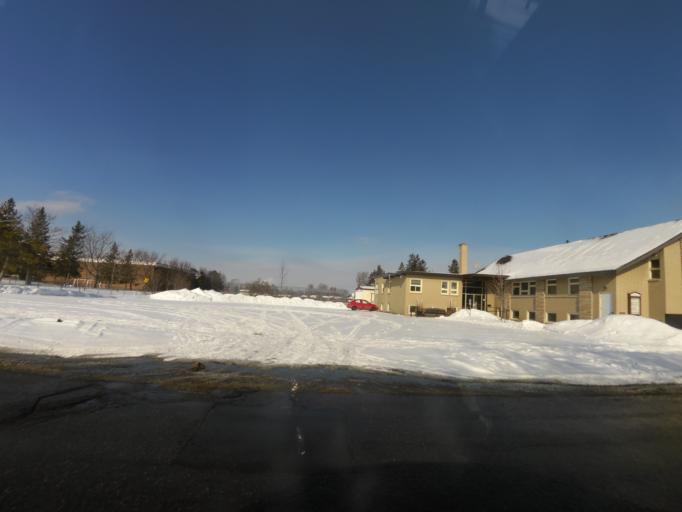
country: CA
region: Ontario
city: Ottawa
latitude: 45.3892
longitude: -75.6280
